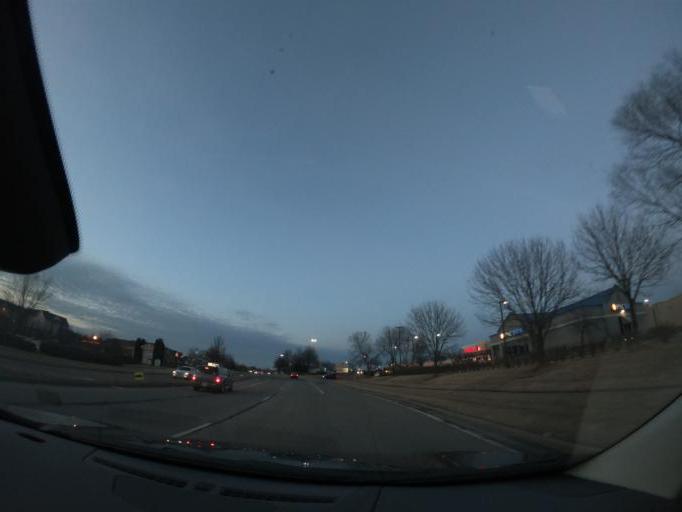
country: US
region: Kentucky
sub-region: Jefferson County
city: Worthington
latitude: 38.2960
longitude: -85.5600
